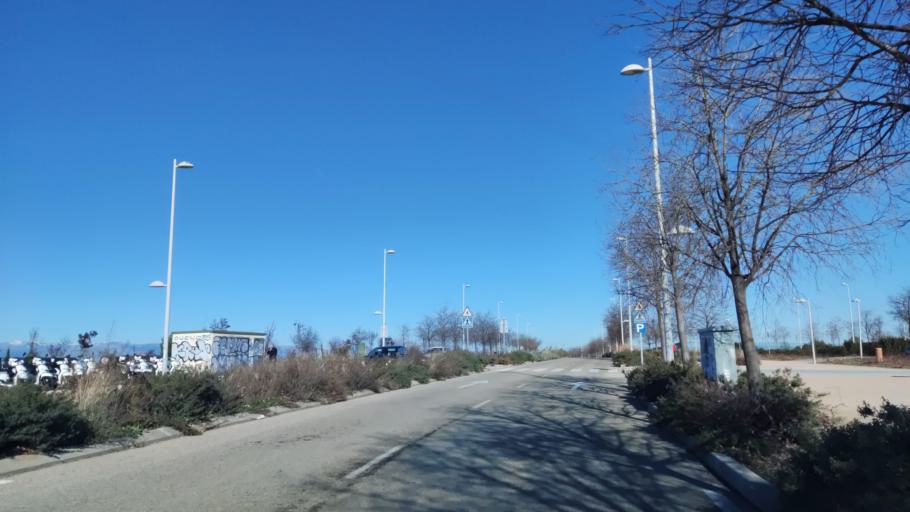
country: ES
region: Madrid
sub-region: Provincia de Madrid
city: Hortaleza
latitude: 40.4851
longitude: -3.6424
